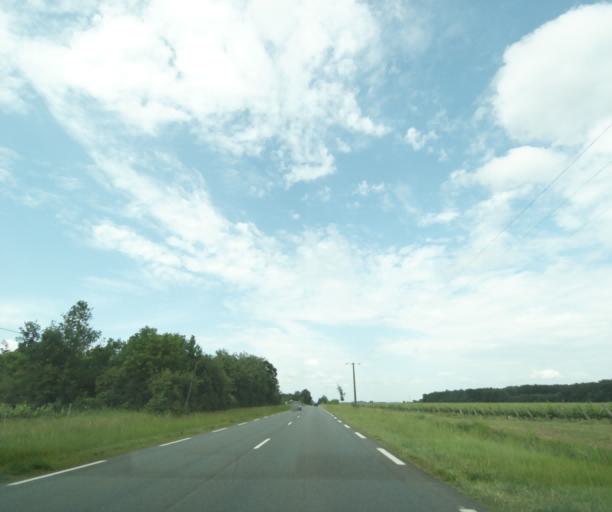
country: FR
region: Pays de la Loire
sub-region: Departement de Maine-et-Loire
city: Montreuil-Bellay
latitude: 47.1533
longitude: -0.1477
